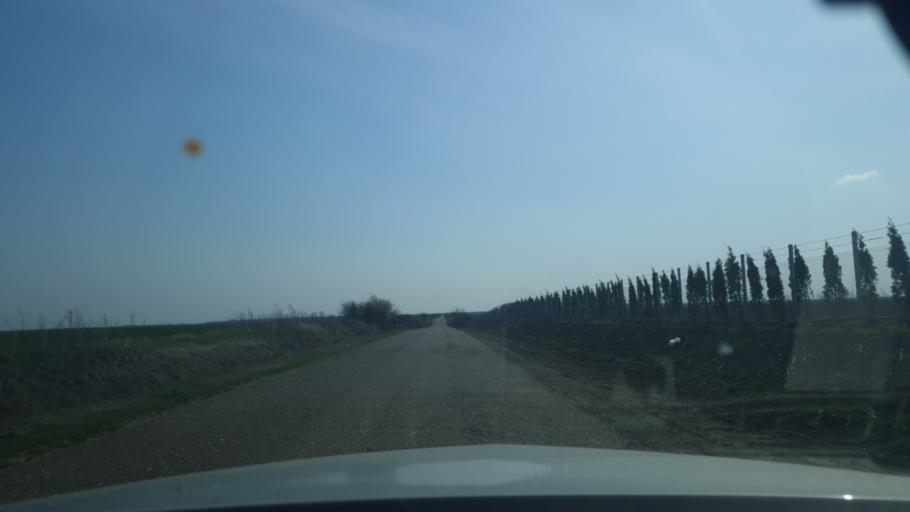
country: RS
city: Putinci
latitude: 45.0394
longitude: 19.9579
